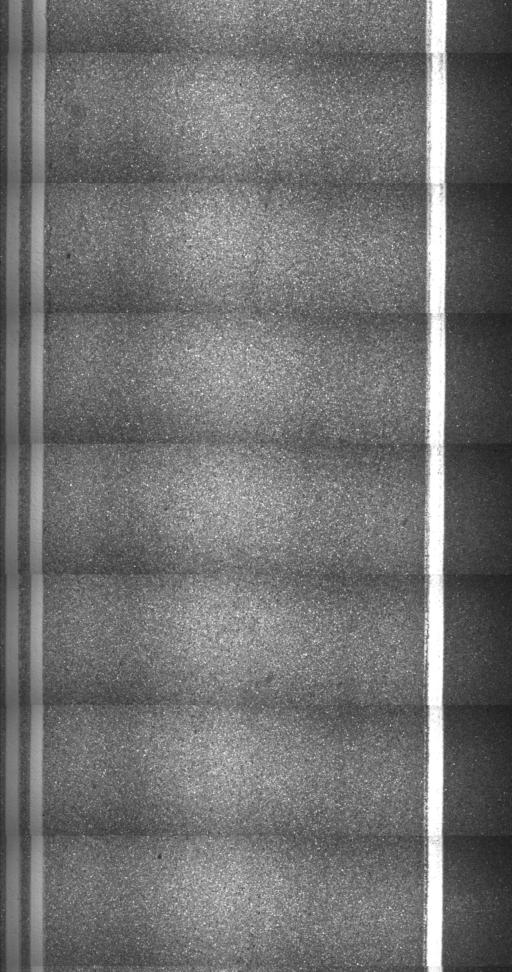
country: US
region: Vermont
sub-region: Windham County
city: Dover
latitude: 42.9271
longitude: -72.8476
